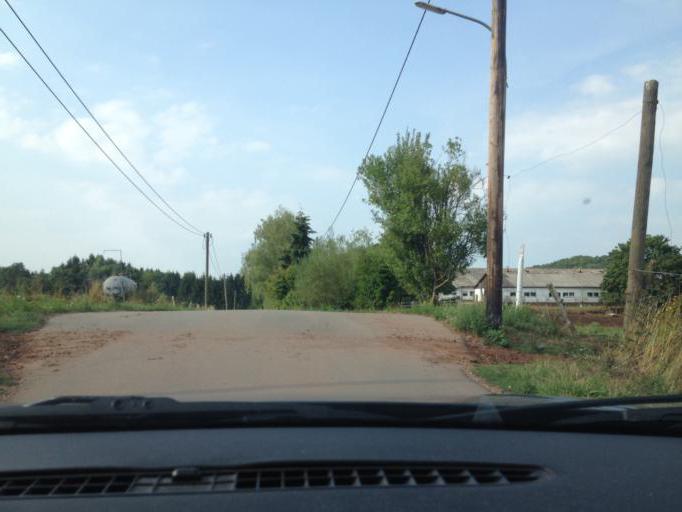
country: DE
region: Saarland
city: Namborn
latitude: 49.5316
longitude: 7.1416
